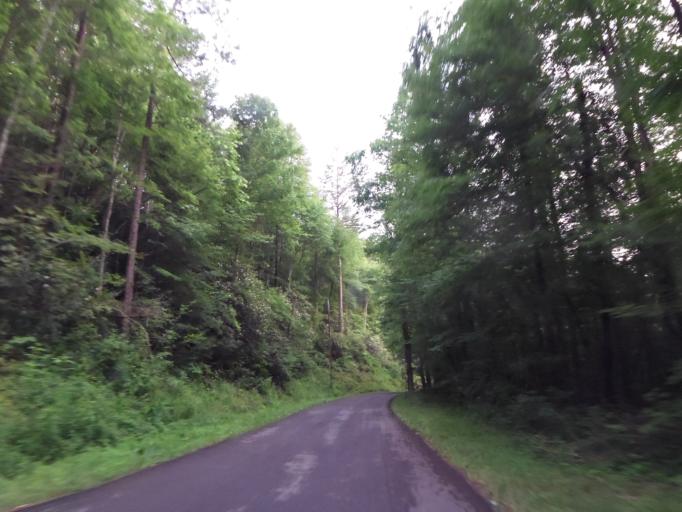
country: US
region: Tennessee
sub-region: Sevier County
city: Seymour
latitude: 35.7448
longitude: -83.7339
